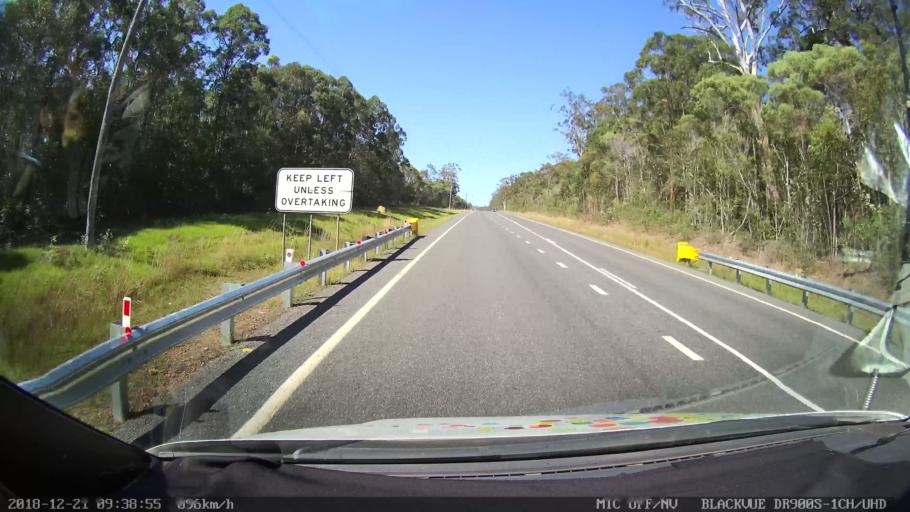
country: AU
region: New South Wales
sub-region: Clarence Valley
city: Grafton
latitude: -29.5553
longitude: 152.9784
